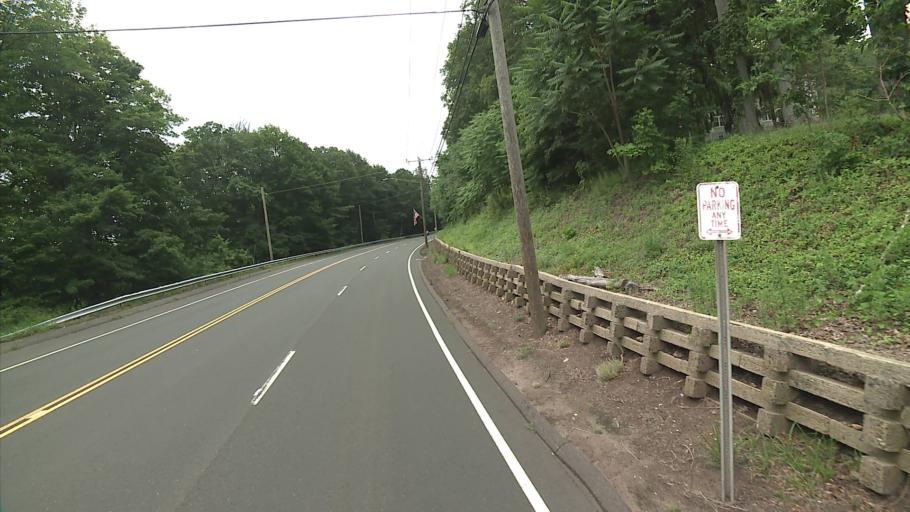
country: US
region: Connecticut
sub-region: Middlesex County
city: Cromwell
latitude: 41.6062
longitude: -72.6487
